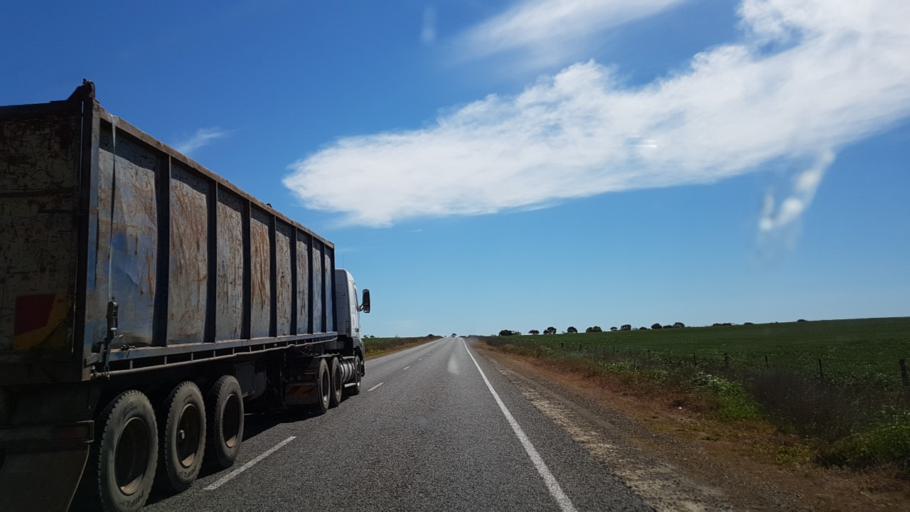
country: AU
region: South Australia
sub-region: Light
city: Kapunda
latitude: -34.2231
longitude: 138.7394
